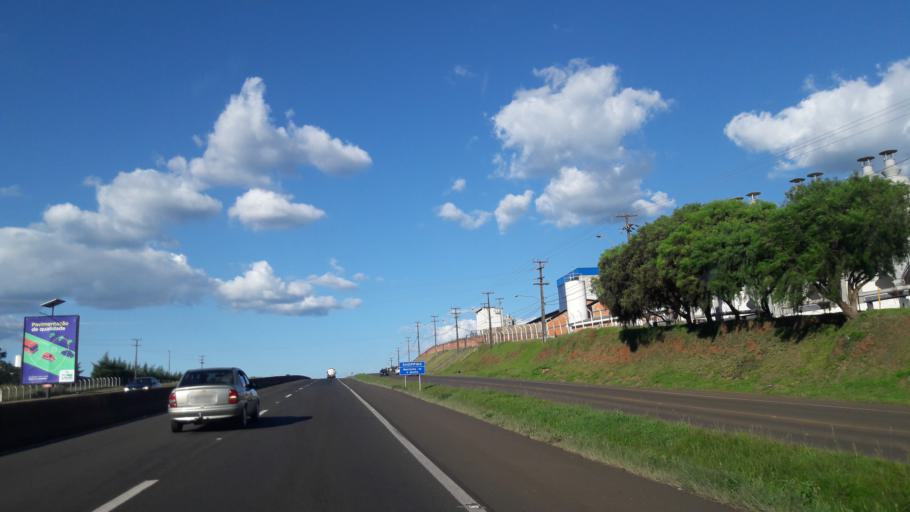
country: BR
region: Parana
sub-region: Guarapuava
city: Guarapuava
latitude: -25.3555
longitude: -51.4615
